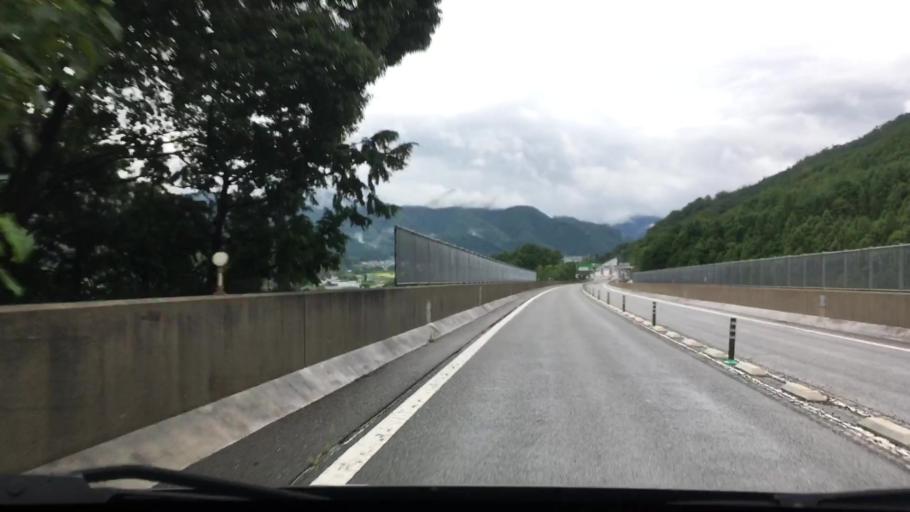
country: JP
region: Hyogo
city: Toyooka
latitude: 35.2915
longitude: 134.8243
